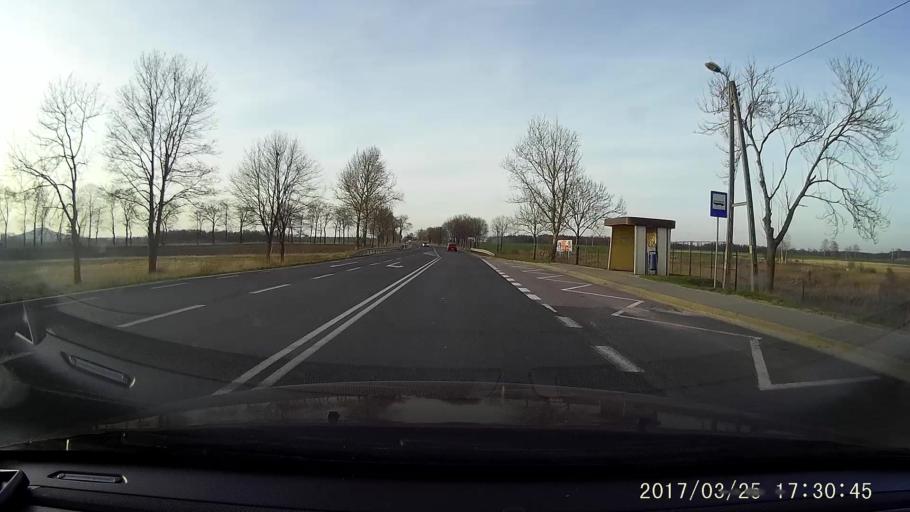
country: PL
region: Lower Silesian Voivodeship
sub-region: Powiat zgorzelecki
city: Sulikow
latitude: 51.0950
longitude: 15.0219
